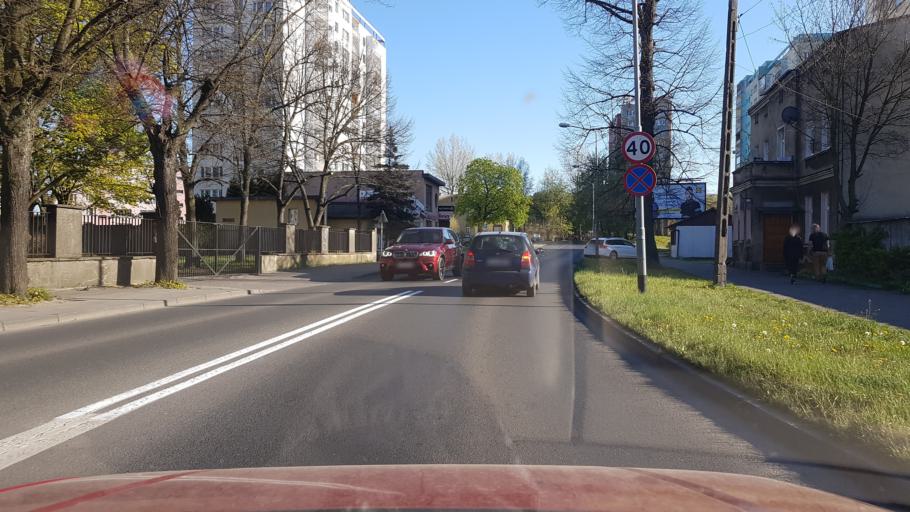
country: PL
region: West Pomeranian Voivodeship
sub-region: Szczecin
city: Szczecin
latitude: 53.3815
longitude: 14.6355
